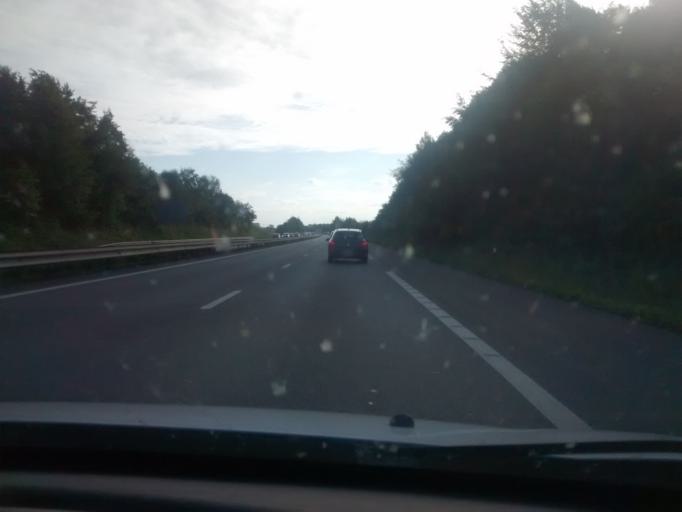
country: FR
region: Brittany
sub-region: Departement d'Ille-et-Vilaine
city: Erbree
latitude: 48.0838
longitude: -1.1287
